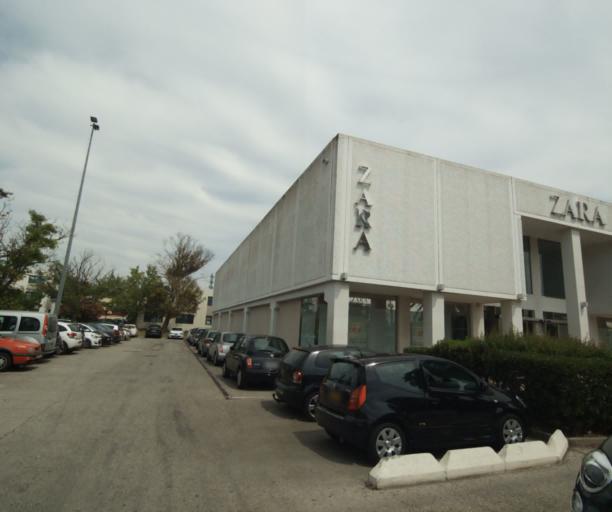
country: FR
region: Provence-Alpes-Cote d'Azur
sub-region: Departement du Var
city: La Garde
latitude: 43.1412
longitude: 6.0179
